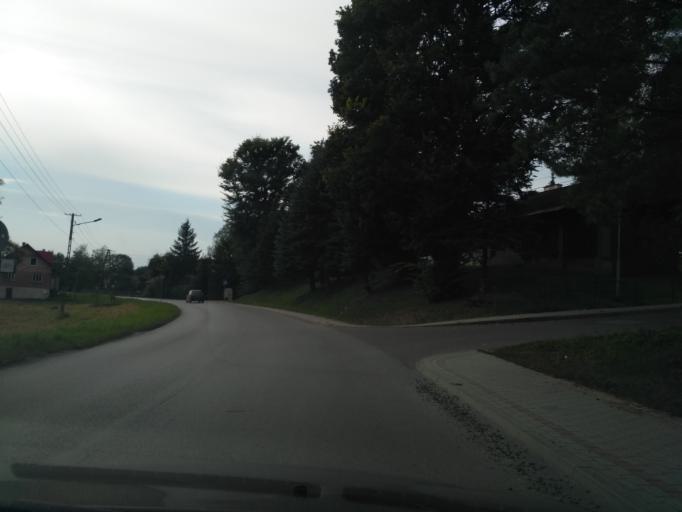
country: PL
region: Subcarpathian Voivodeship
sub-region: Powiat rzeszowski
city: Zglobien
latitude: 50.0123
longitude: 21.8550
